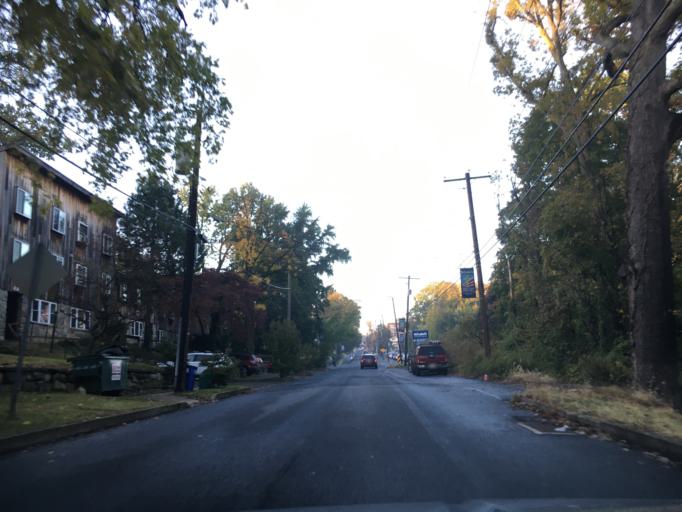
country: US
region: Pennsylvania
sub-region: Lehigh County
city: Fountain Hill
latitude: 40.6116
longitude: -75.3898
